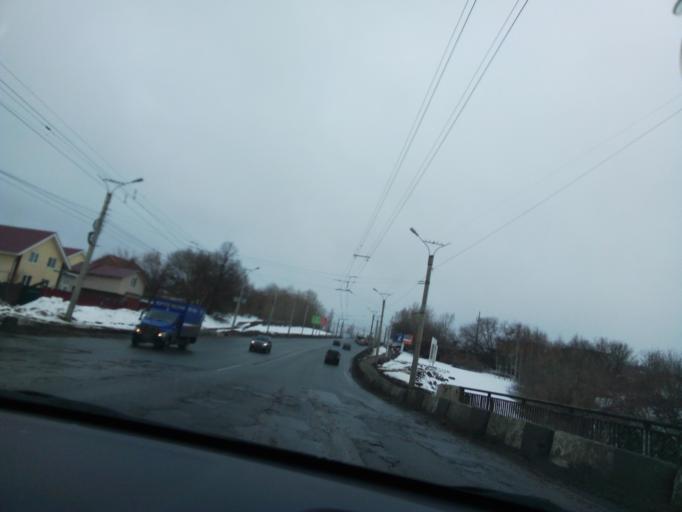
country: RU
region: Chuvashia
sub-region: Cheboksarskiy Rayon
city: Cheboksary
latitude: 56.1260
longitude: 47.2174
